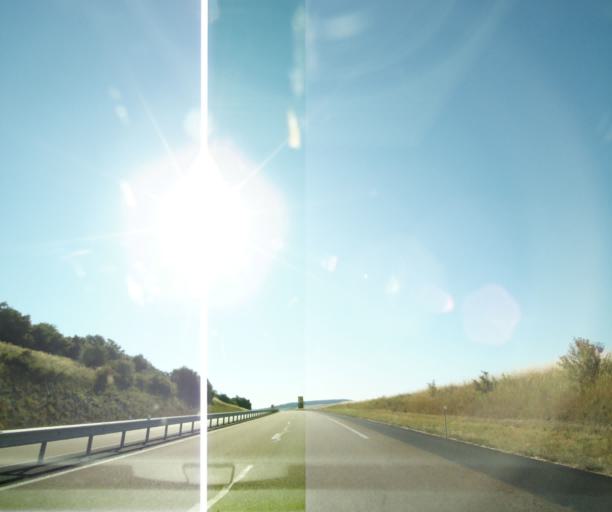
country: FR
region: Champagne-Ardenne
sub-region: Departement de l'Aube
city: Estissac
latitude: 48.2720
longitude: 3.8265
